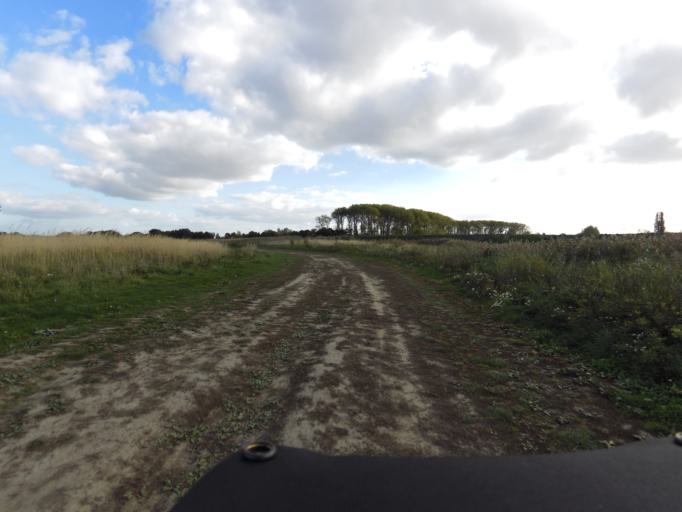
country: NL
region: North Brabant
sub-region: Gemeente Steenbergen
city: Steenbergen
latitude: 51.6026
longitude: 4.3071
